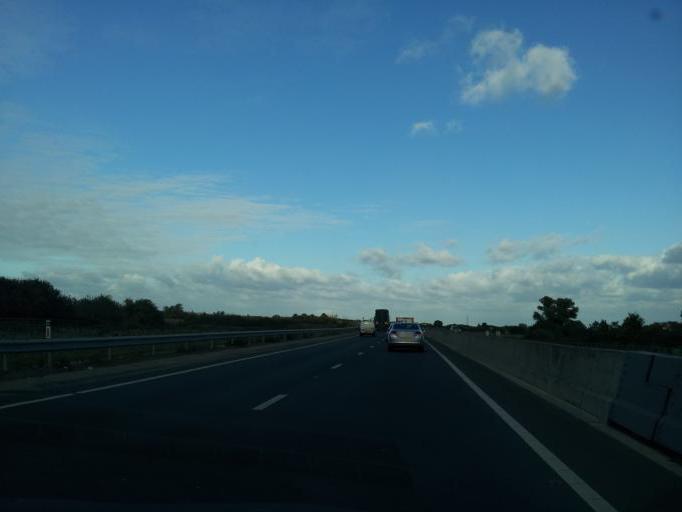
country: GB
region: England
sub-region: Central Bedfordshire
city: Lidlington
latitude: 52.0532
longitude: -0.5769
